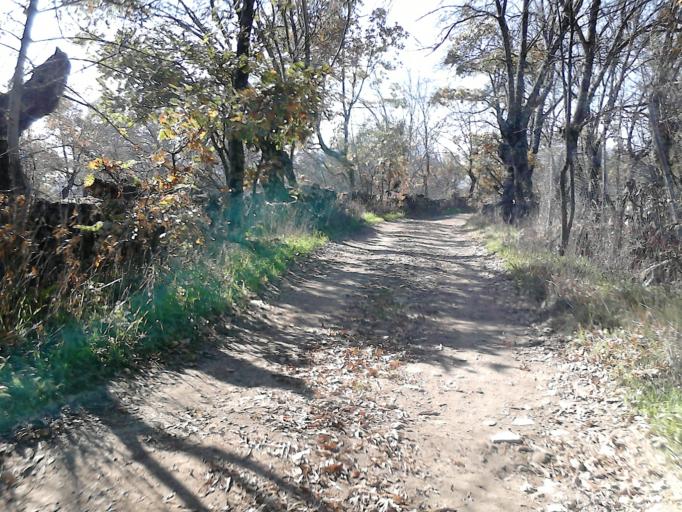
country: ES
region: Madrid
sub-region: Provincia de Madrid
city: El Escorial
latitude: 40.5976
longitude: -4.1070
